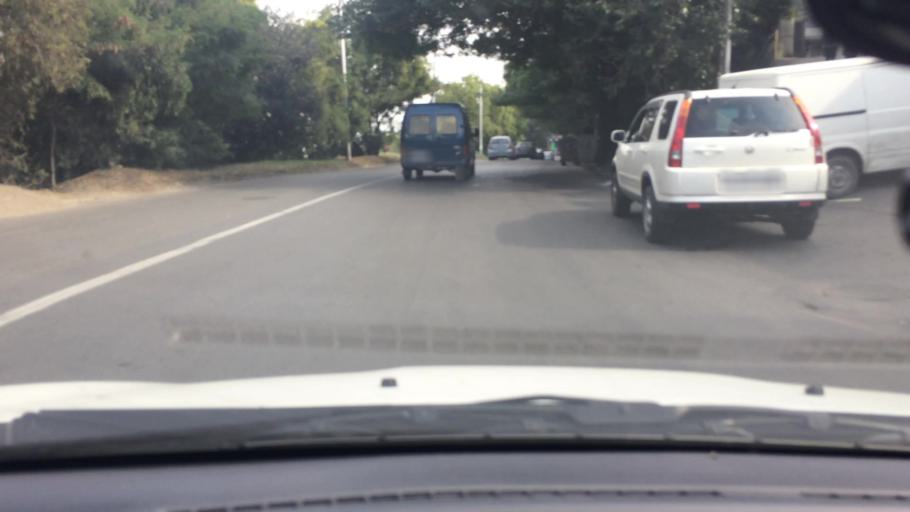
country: GE
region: T'bilisi
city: Tbilisi
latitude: 41.6716
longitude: 44.8371
